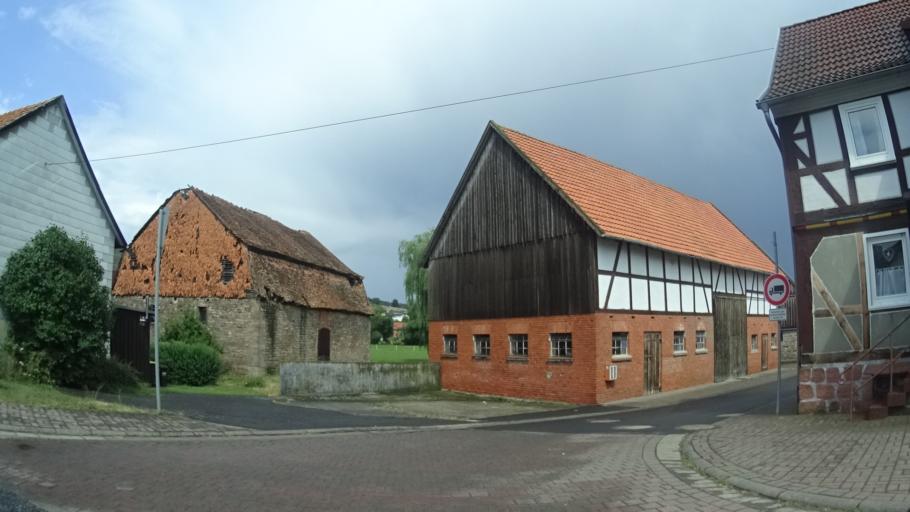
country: DE
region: Hesse
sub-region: Regierungsbezirk Giessen
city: Lauterbach
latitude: 50.6288
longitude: 9.4442
